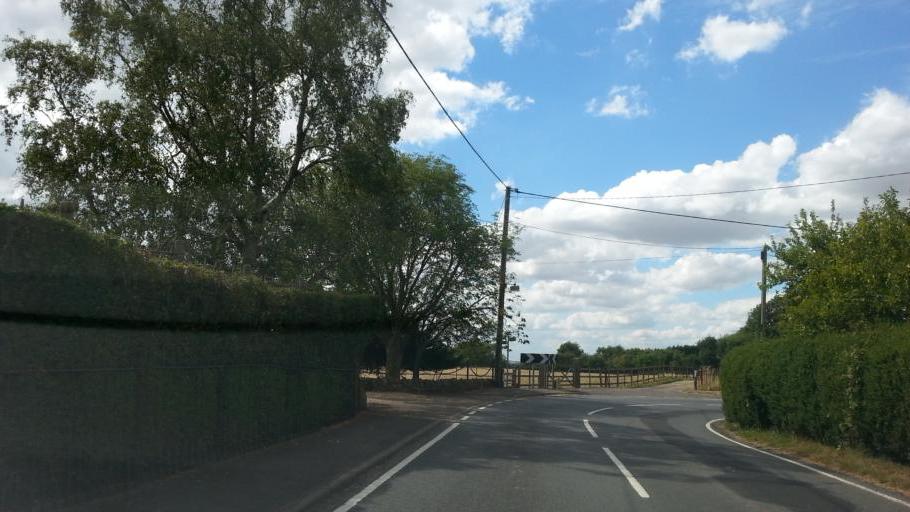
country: GB
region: England
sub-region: Northamptonshire
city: Silverstone
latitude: 52.0909
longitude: -0.9934
